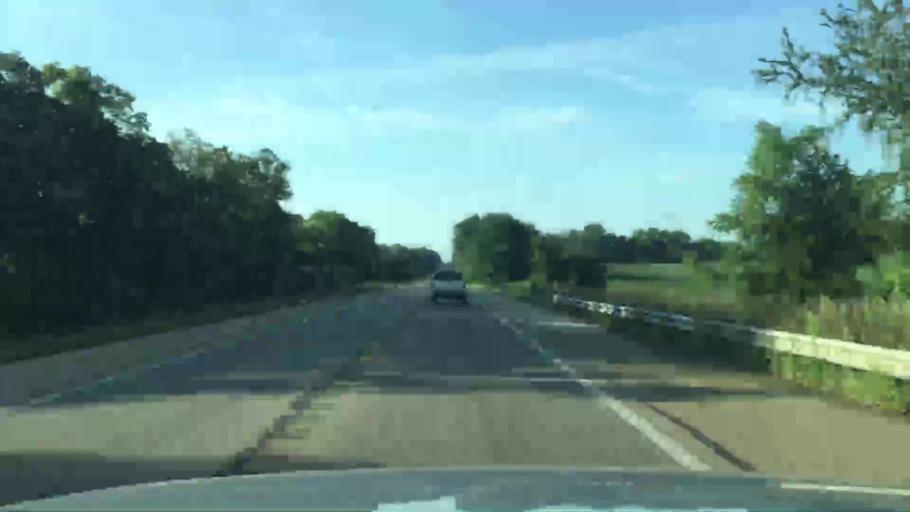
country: US
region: Michigan
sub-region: Jackson County
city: Vandercook Lake
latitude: 42.0999
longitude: -84.3639
